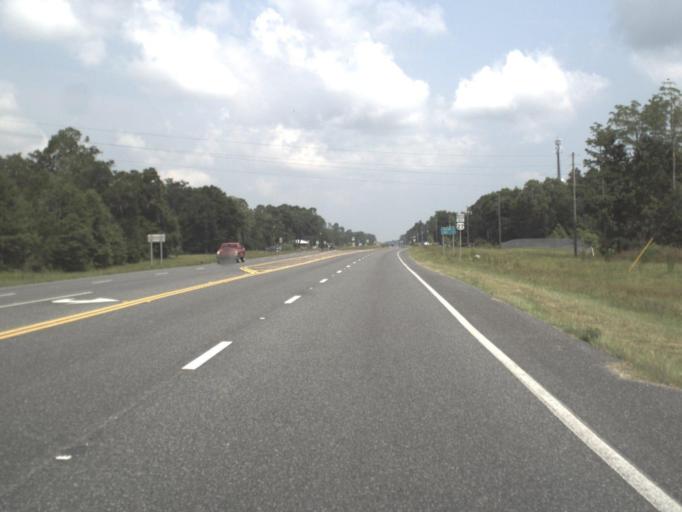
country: US
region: Florida
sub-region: Levy County
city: Bronson
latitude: 29.4482
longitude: -82.6433
